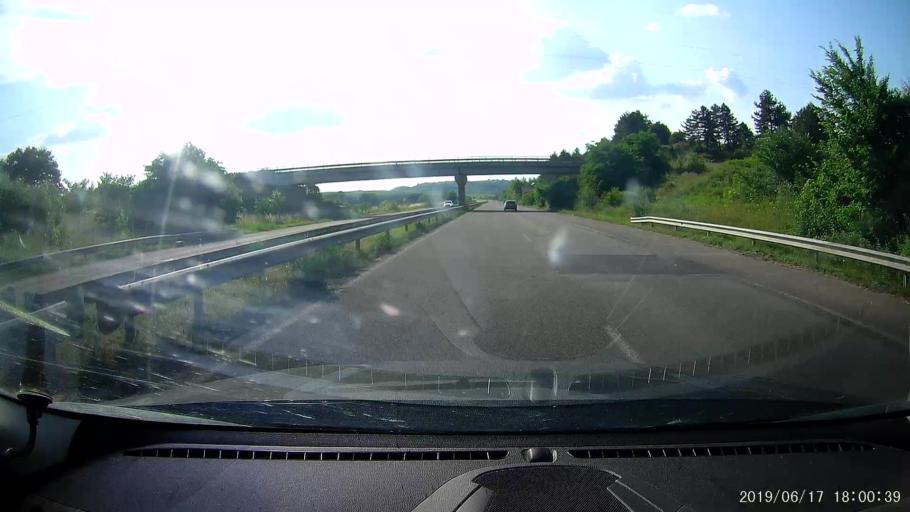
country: BG
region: Khaskovo
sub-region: Obshtina Svilengrad
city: Svilengrad
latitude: 41.7389
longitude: 26.2748
